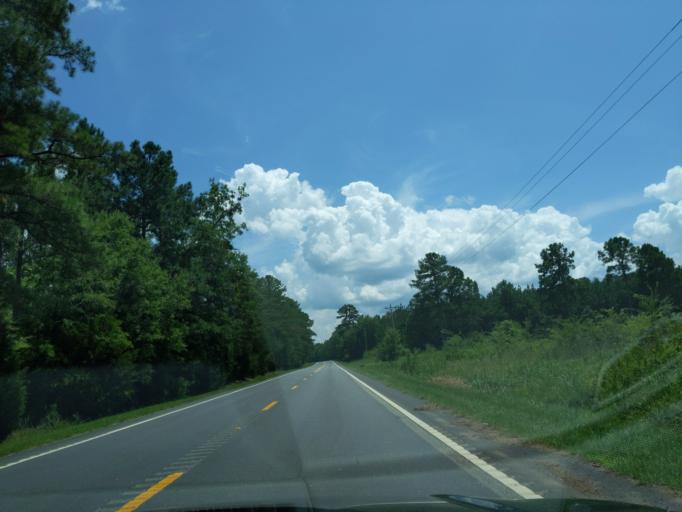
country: US
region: South Carolina
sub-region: Edgefield County
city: Edgefield
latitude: 33.8556
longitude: -81.9828
